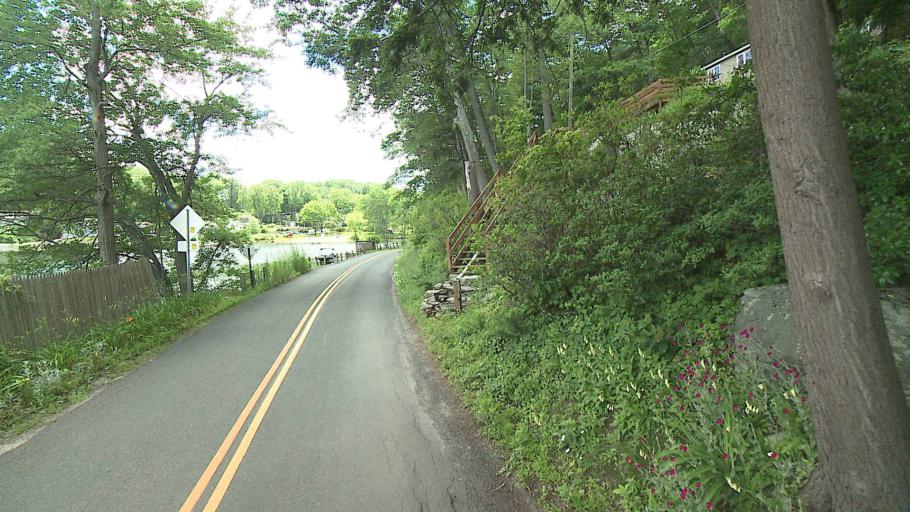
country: US
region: Connecticut
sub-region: Litchfield County
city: New Preston
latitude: 41.6845
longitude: -73.3534
